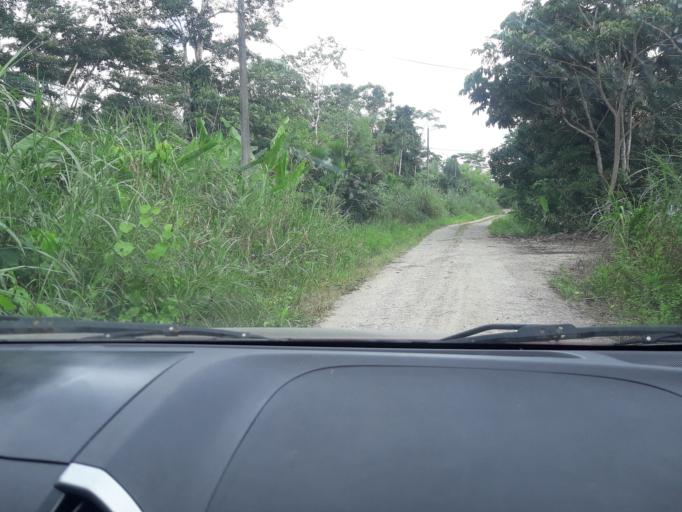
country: EC
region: Napo
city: Tena
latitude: -1.0957
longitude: -77.6752
